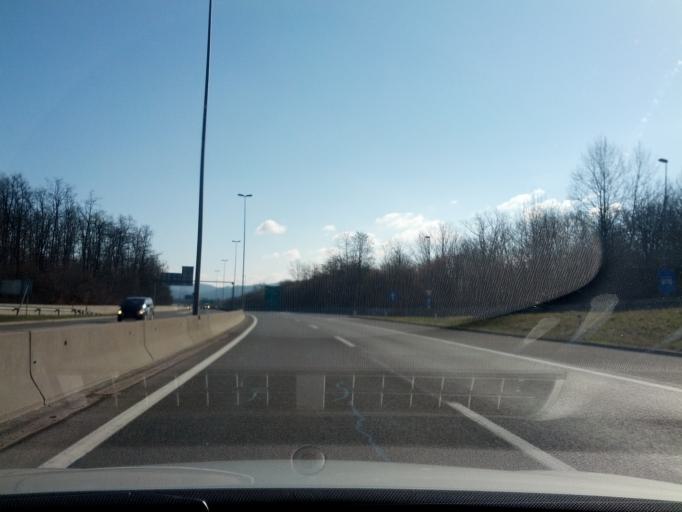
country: SI
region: Dol pri Ljubljani
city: Dol pri Ljubljani
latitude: 46.0674
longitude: 14.5591
